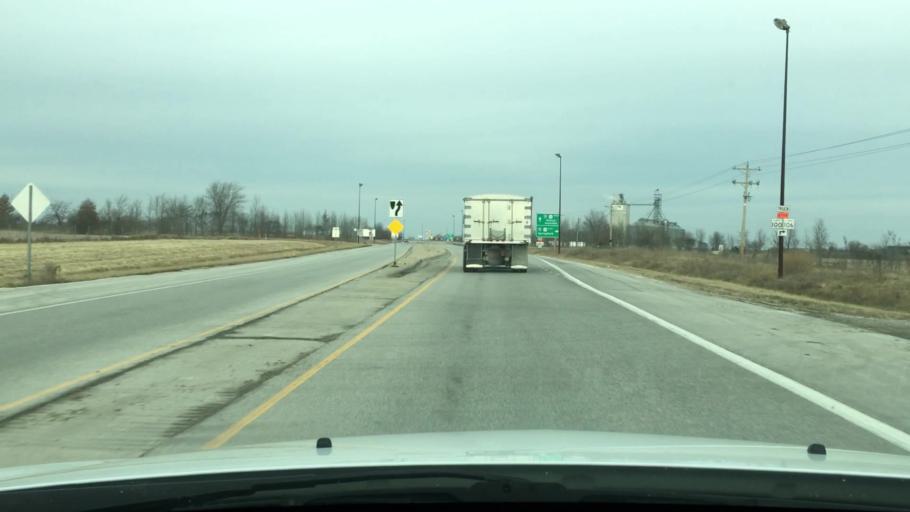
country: US
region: Illinois
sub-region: Pike County
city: Griggsville
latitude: 39.6710
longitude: -90.7692
